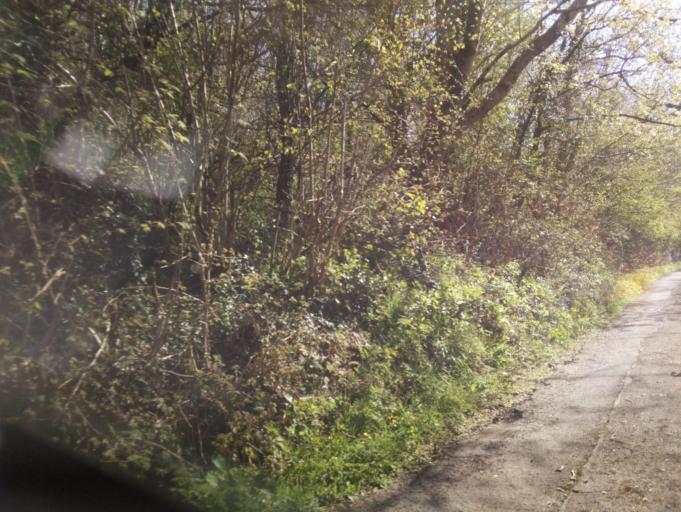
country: GB
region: Wales
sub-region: Monmouthshire
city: Llangwm
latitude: 51.6848
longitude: -2.8128
